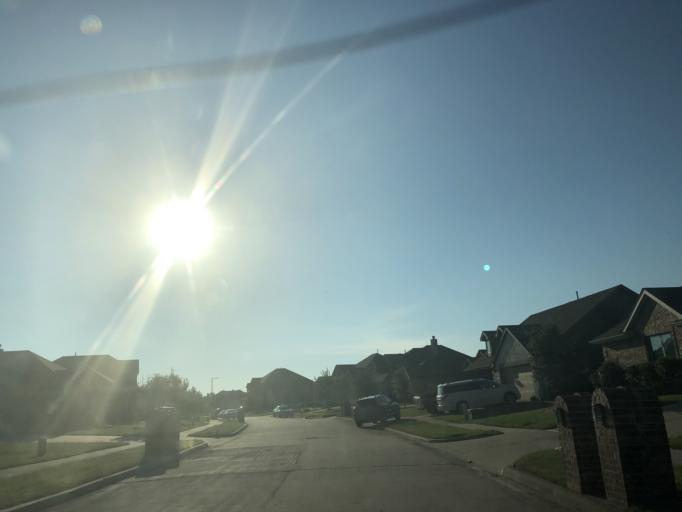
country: US
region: Texas
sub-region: Dallas County
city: Sunnyvale
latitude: 32.8450
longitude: -96.5591
